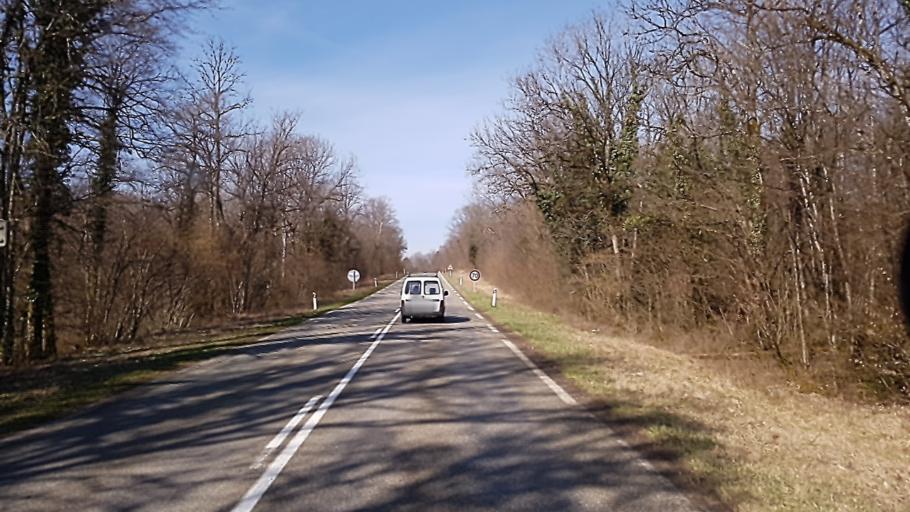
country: FR
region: Franche-Comte
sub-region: Departement du Jura
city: Poligny
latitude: 46.8160
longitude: 5.7764
